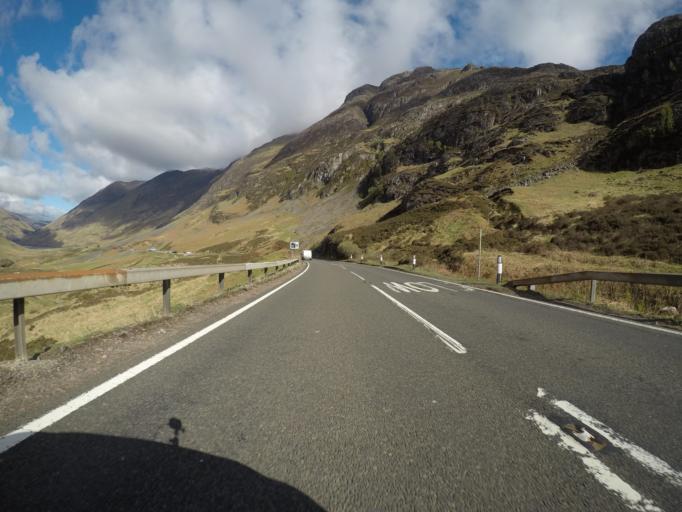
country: GB
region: Scotland
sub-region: Highland
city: Fort William
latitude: 56.6668
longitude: -4.9827
